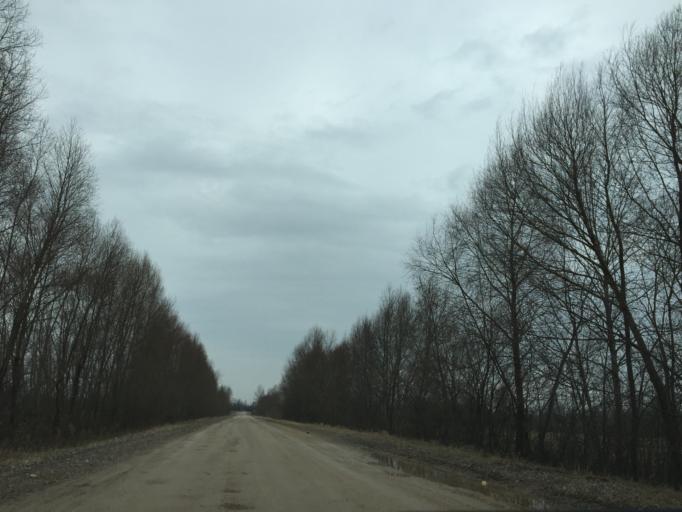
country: LV
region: Jelgava
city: Jelgava
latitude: 56.6963
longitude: 23.7237
